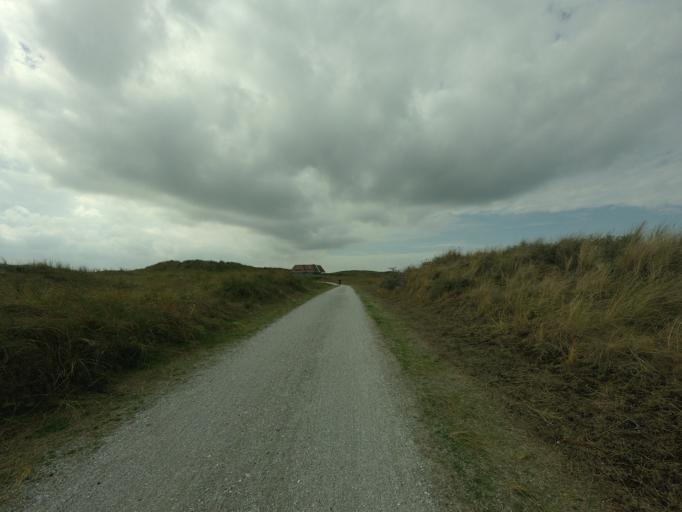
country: NL
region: Friesland
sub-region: Gemeente Ameland
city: Nes
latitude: 53.4609
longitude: 5.8110
